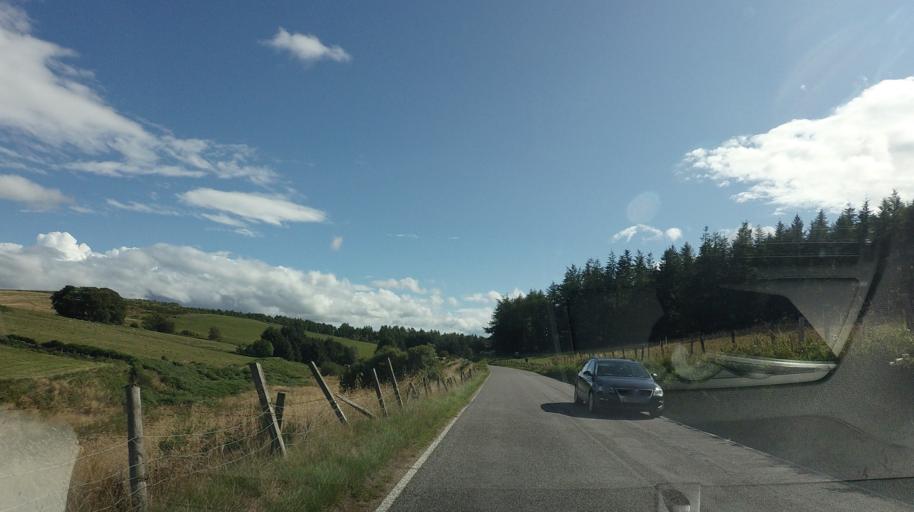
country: GB
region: Scotland
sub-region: Aberdeenshire
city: Torphins
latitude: 57.1354
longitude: -2.7040
